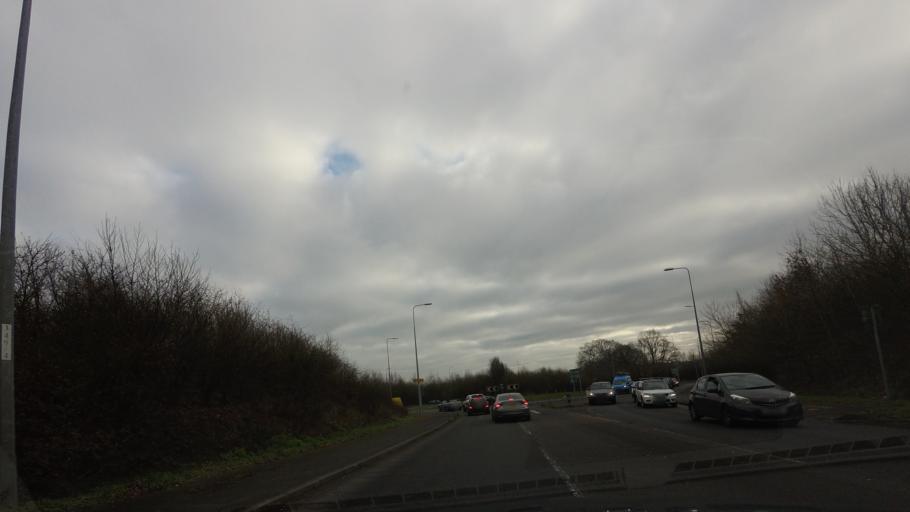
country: GB
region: England
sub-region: Kent
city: Paddock Wood
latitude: 51.1109
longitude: 0.4006
